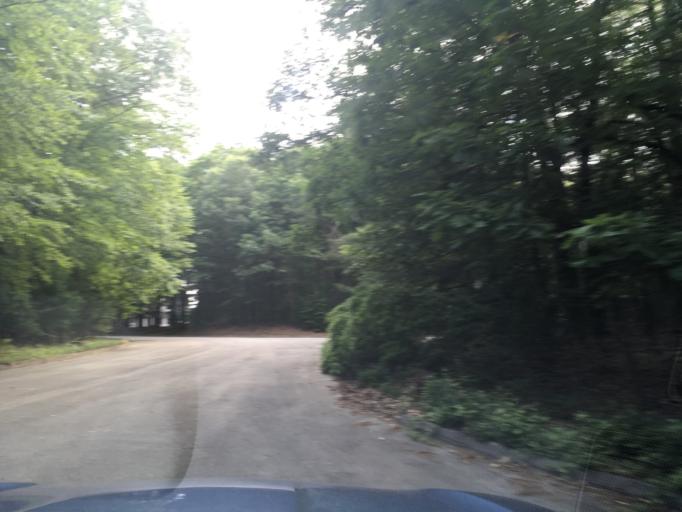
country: US
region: Rhode Island
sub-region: Washington County
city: Exeter
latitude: 41.6322
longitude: -71.5377
